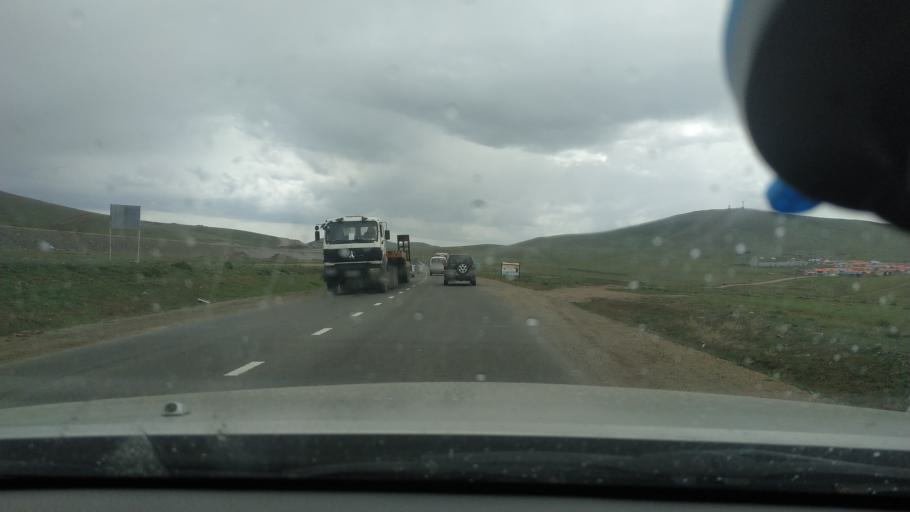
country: MN
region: Ulaanbaatar
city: Ulaanbaatar
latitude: 47.8001
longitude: 106.7464
